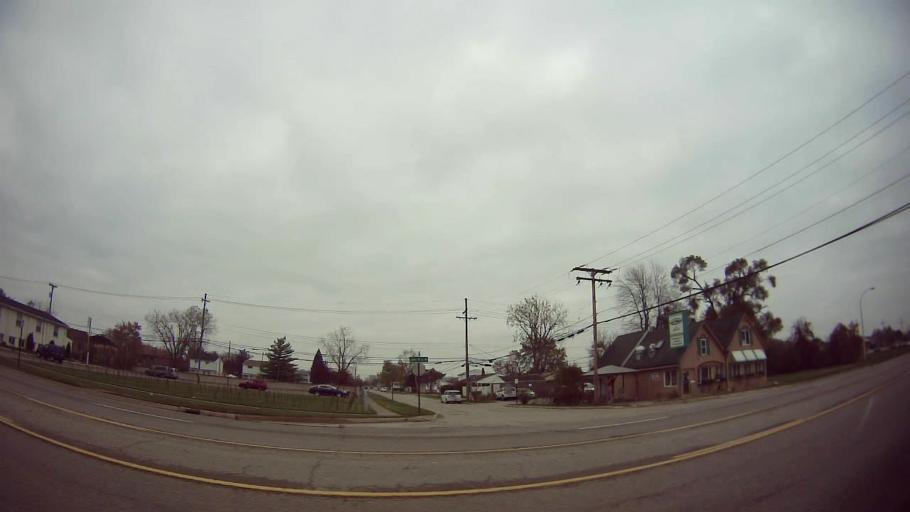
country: US
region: Michigan
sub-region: Oakland County
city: Madison Heights
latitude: 42.5178
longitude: -83.1064
